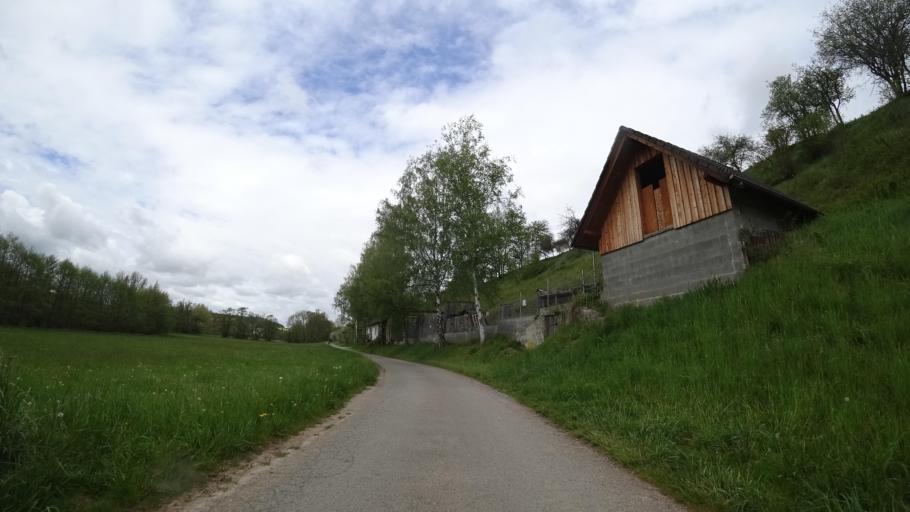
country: DE
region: Hesse
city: Liebenau
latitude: 51.4603
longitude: 9.3183
